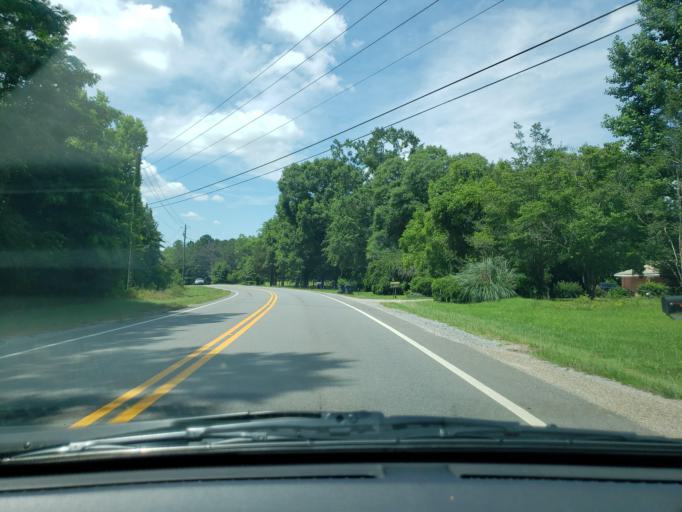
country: US
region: Alabama
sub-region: Elmore County
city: Eclectic
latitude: 32.6219
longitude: -85.9476
